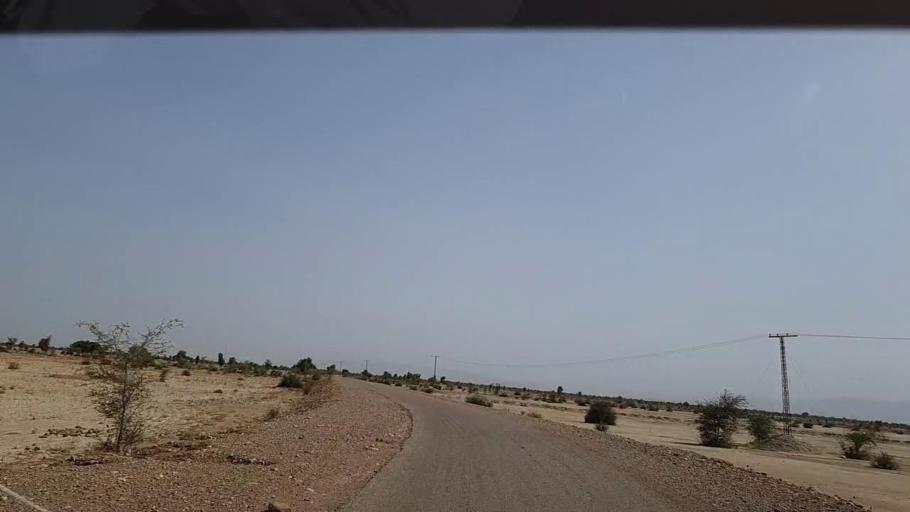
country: PK
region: Sindh
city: Johi
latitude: 26.6616
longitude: 67.5064
